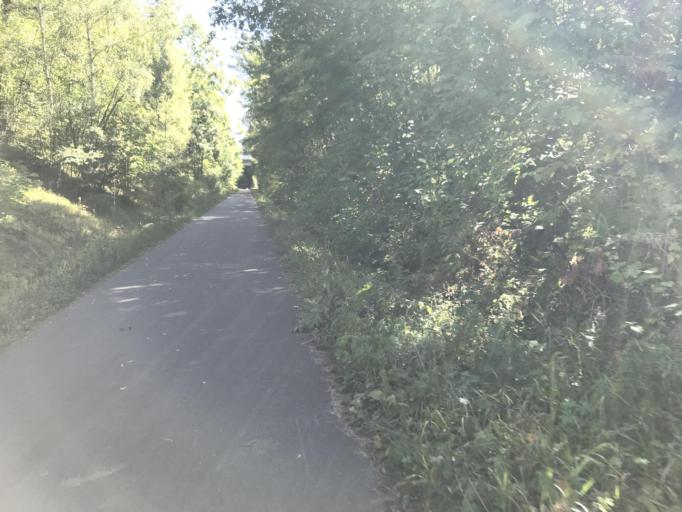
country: DE
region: Hesse
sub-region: Regierungsbezirk Kassel
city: Korbach
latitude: 51.2609
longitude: 8.9033
